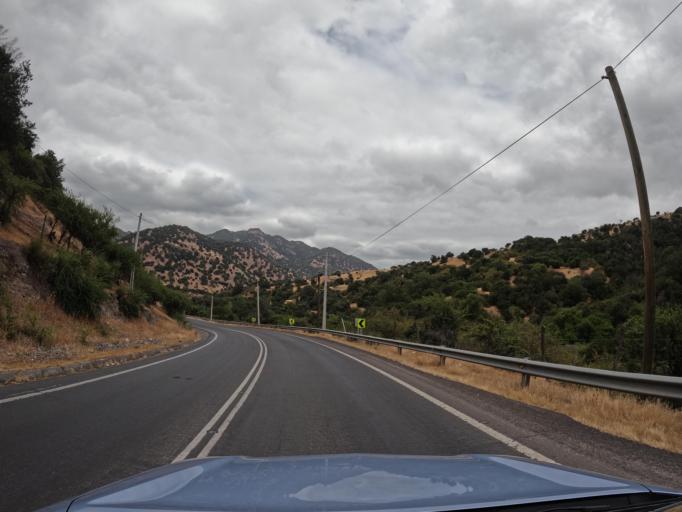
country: CL
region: Maule
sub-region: Provincia de Curico
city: Teno
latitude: -34.8158
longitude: -71.2044
